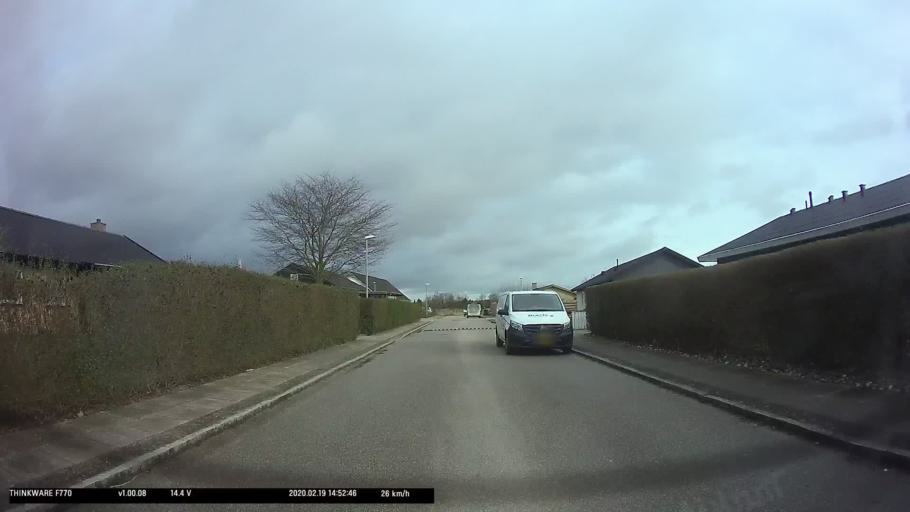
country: DK
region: Capital Region
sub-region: Tarnby Kommune
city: Tarnby
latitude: 55.5883
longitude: 12.5758
